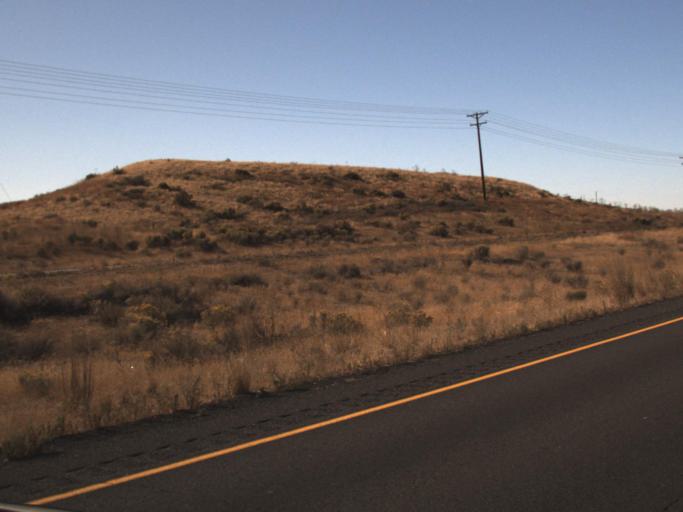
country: US
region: Washington
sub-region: Franklin County
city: Pasco
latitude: 46.4233
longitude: -119.0330
